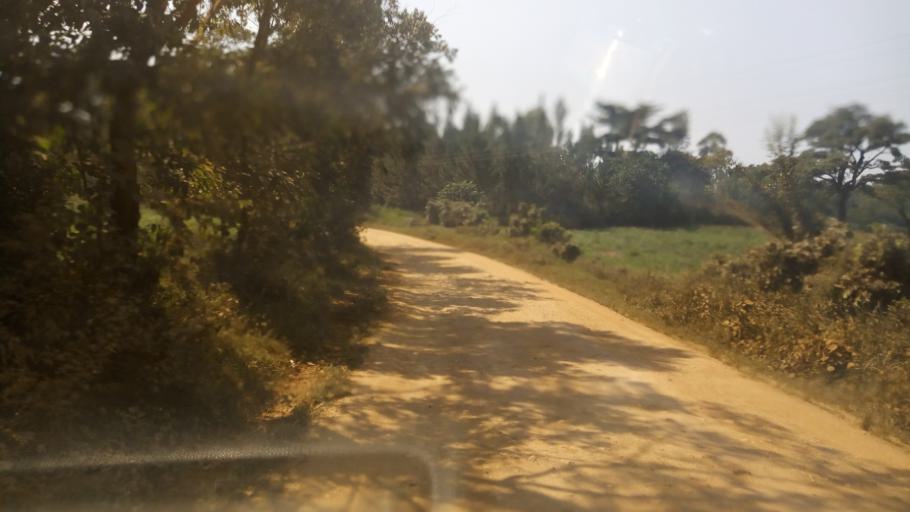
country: UG
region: Western Region
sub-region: Kanungu District
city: Ntungamo
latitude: -0.9133
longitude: 29.6234
